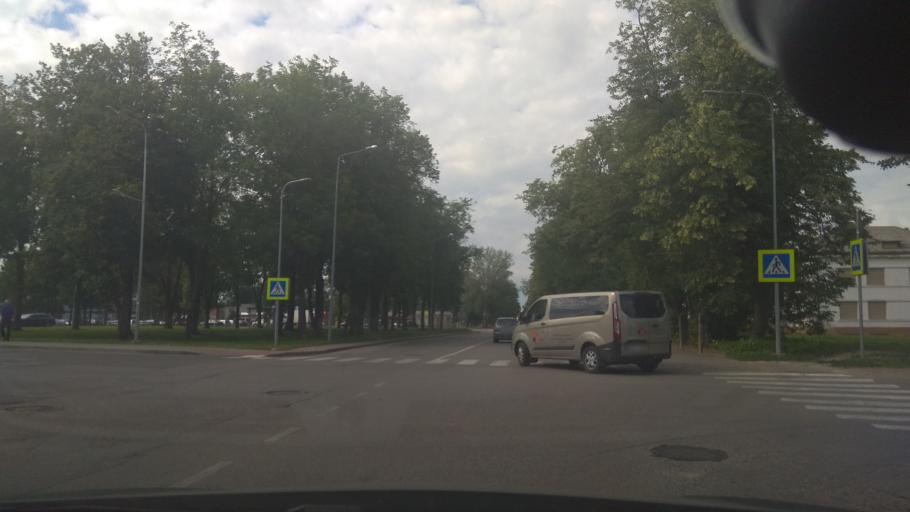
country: LT
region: Marijampoles apskritis
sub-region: Marijampole Municipality
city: Marijampole
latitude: 54.5453
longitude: 23.3481
